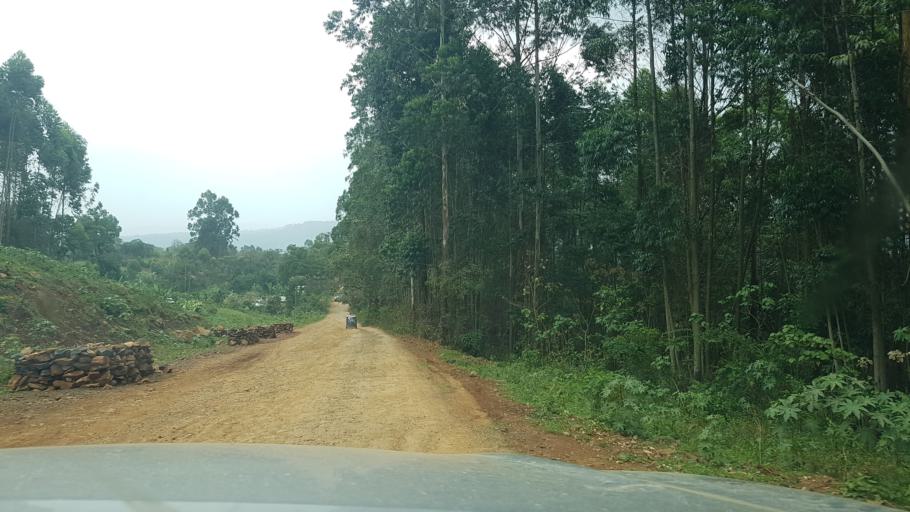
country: ET
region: Oromiya
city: Gore
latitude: 7.8293
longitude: 35.4660
